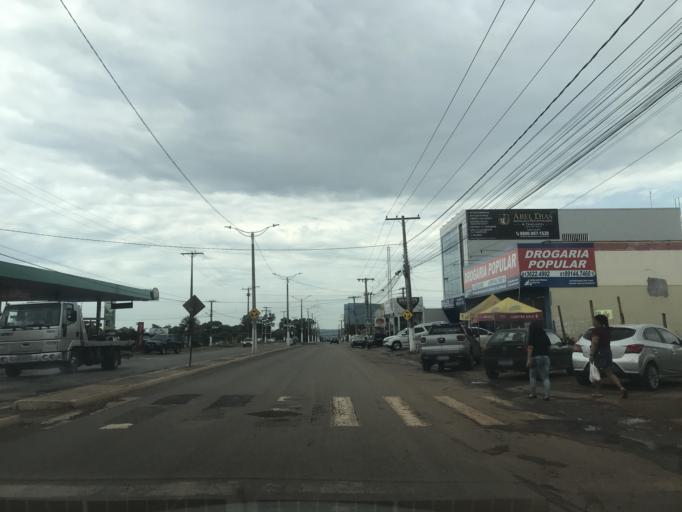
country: BR
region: Goias
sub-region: Luziania
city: Luziania
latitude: -16.2376
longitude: -47.9424
